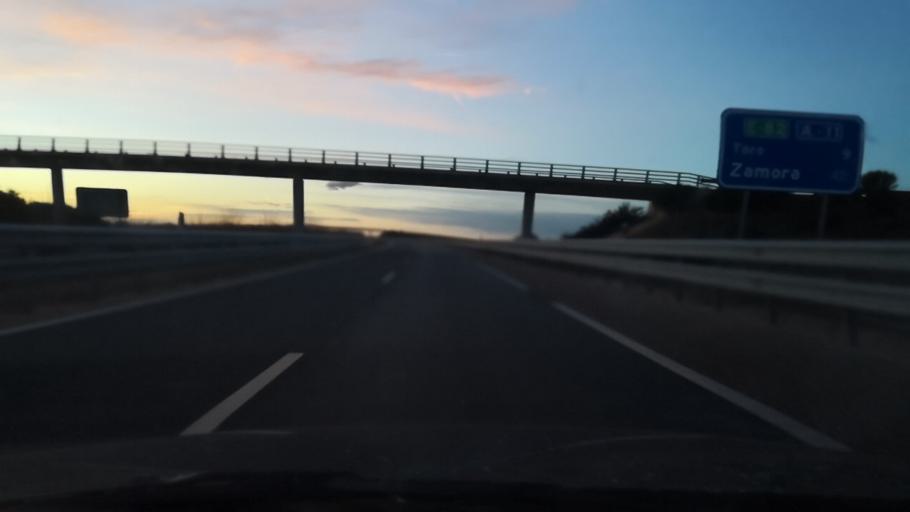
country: ES
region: Castille and Leon
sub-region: Provincia de Zamora
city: Morales de Toro
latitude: 41.5439
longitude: -5.2983
